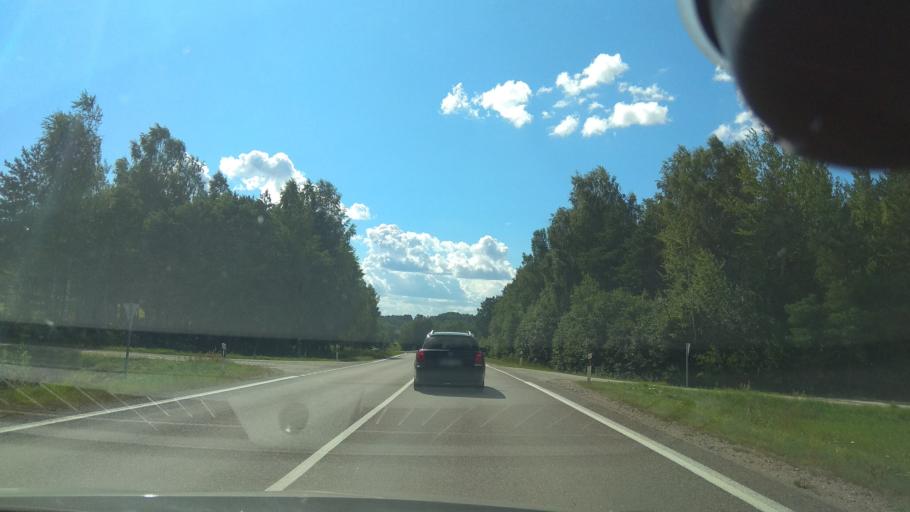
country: LT
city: Vieksniai
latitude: 56.0007
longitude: 22.5459
